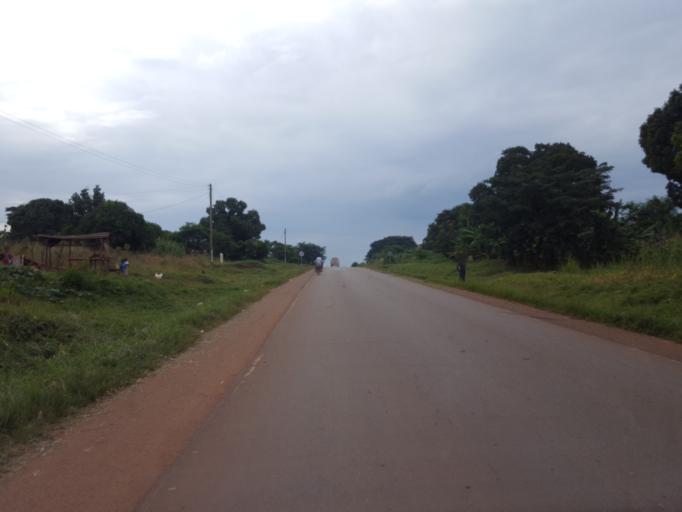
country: UG
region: Central Region
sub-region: Kyankwanzi District
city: Kyankwanzi
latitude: 1.1237
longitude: 31.5976
